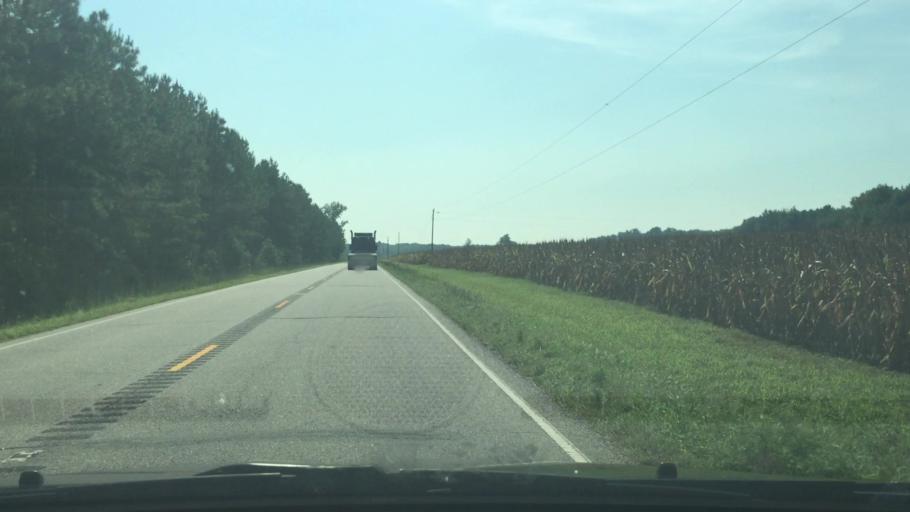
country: US
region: Virginia
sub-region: Sussex County
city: Sussex
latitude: 36.9812
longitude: -77.2366
